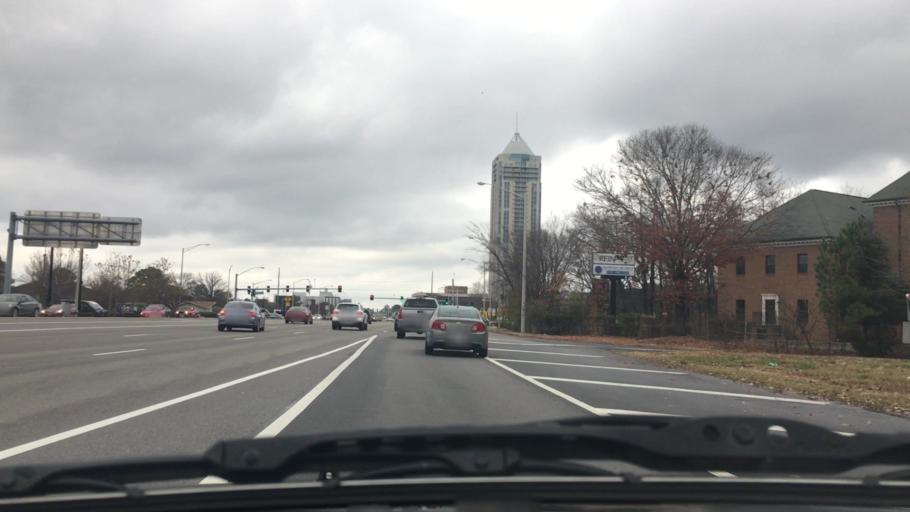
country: US
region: Virginia
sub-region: City of Chesapeake
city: Chesapeake
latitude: 36.8358
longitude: -76.1371
